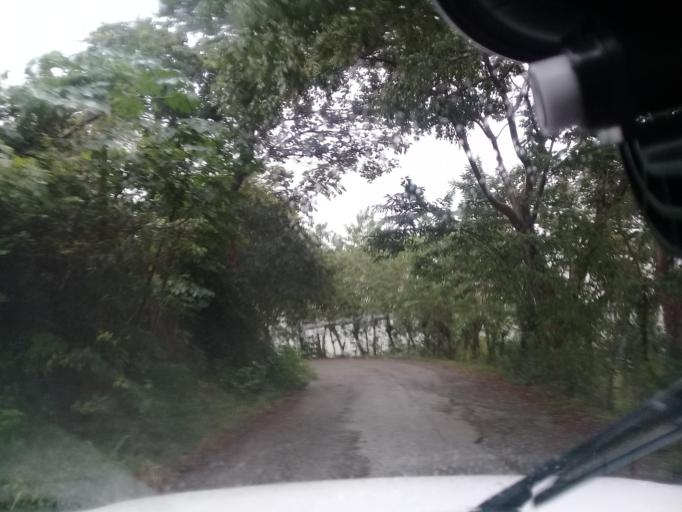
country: MX
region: Veracruz
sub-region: Chalma
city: San Pedro Coyutla
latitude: 21.2179
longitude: -98.4589
